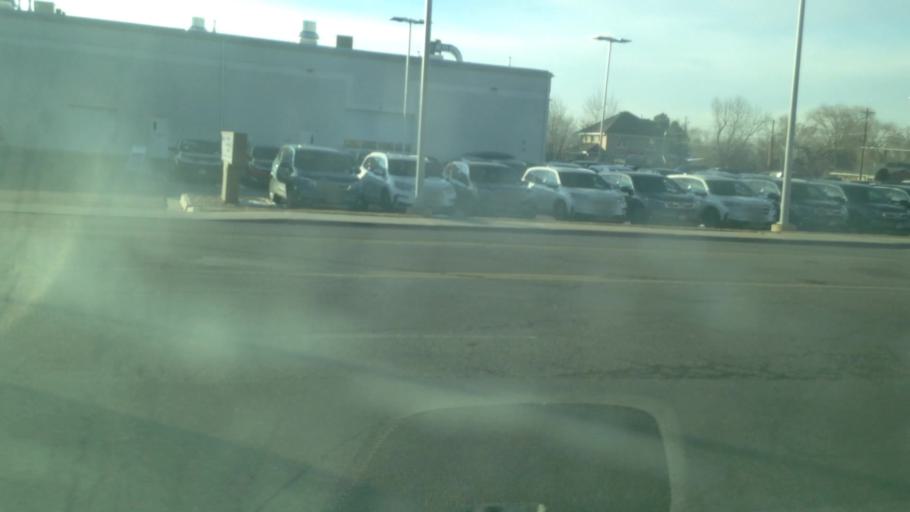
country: US
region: Utah
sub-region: Utah County
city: Orem
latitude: 40.2745
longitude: -111.6902
